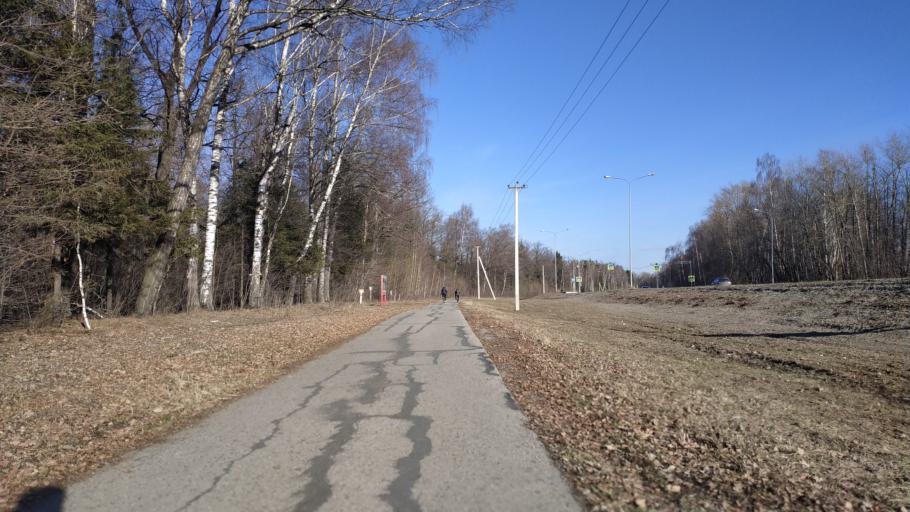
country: RU
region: Chuvashia
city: Ishley
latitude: 56.1329
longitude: 47.1081
